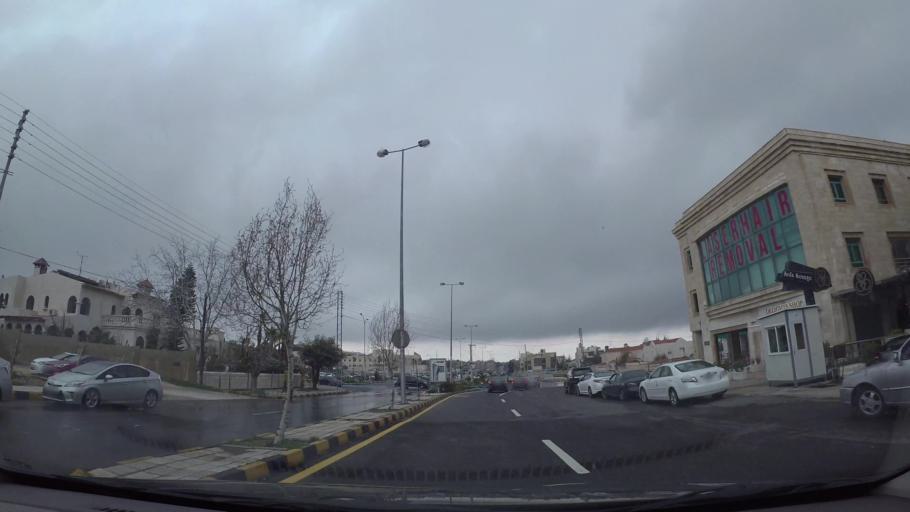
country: JO
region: Amman
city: Al Bunayyat ash Shamaliyah
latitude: 31.9419
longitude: 35.8802
